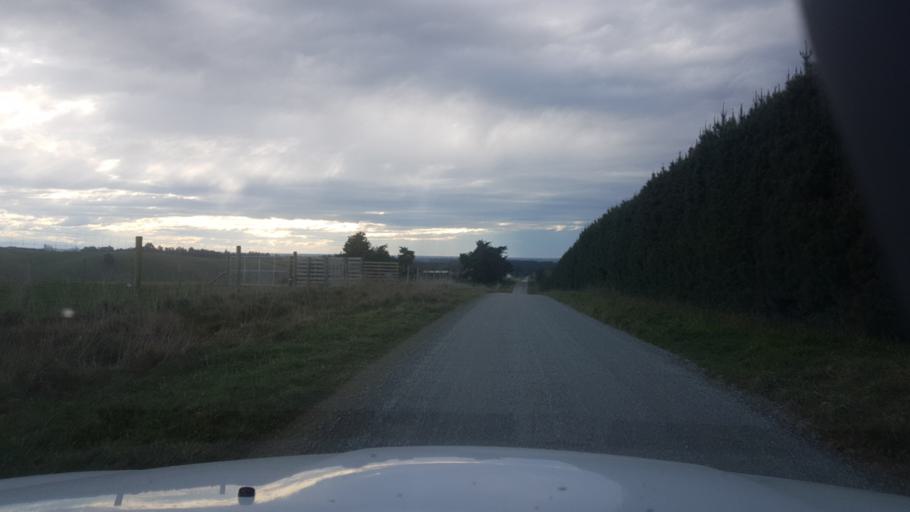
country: NZ
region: Canterbury
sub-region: Timaru District
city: Pleasant Point
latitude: -44.3396
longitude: 171.1452
